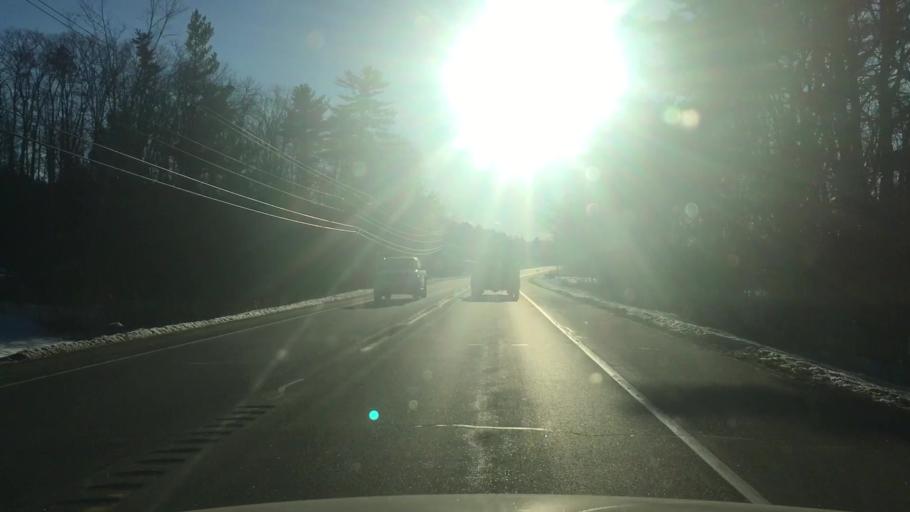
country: US
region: Maine
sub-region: Somerset County
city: Norridgewock
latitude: 44.7353
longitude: -69.7605
